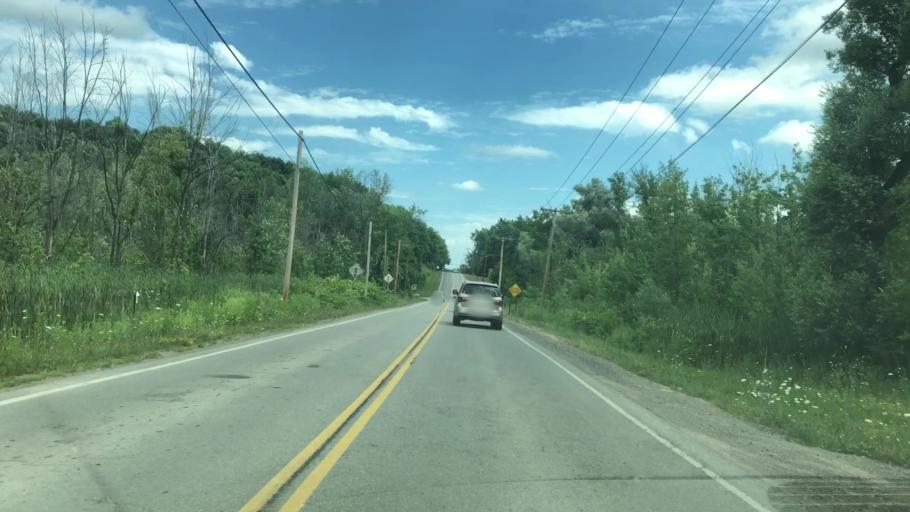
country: US
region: New York
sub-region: Wayne County
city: Macedon
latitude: 43.0770
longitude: -77.3614
